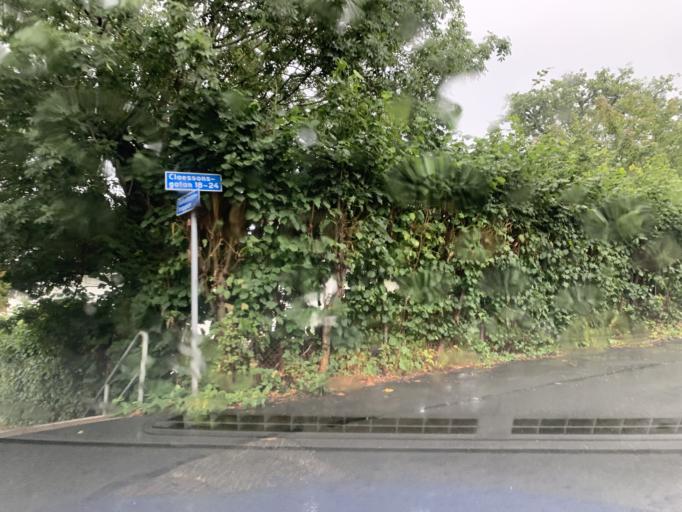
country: SE
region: Vaestra Goetaland
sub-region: Goteborg
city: Goeteborg
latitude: 57.7088
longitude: 12.0195
